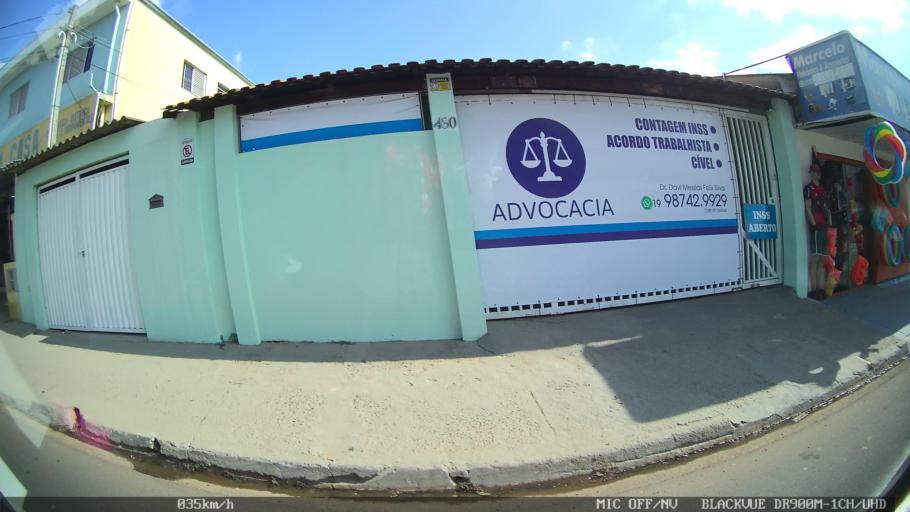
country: BR
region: Sao Paulo
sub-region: Hortolandia
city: Hortolandia
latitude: -22.8811
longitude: -47.2008
